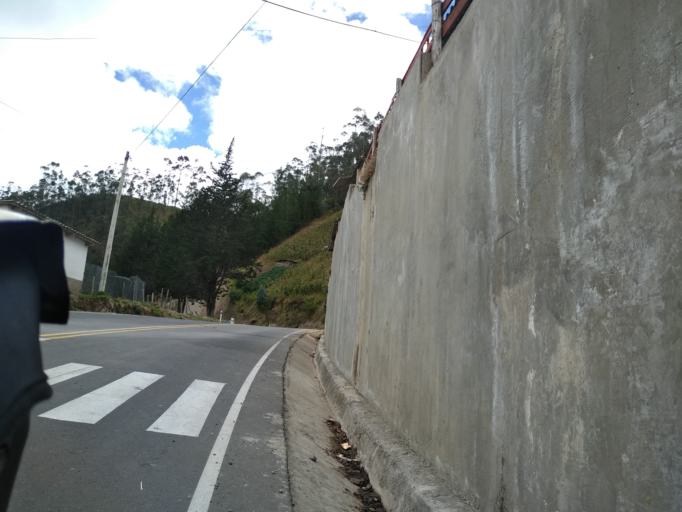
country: EC
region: Cotopaxi
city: Saquisili
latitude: -0.7765
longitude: -78.9092
